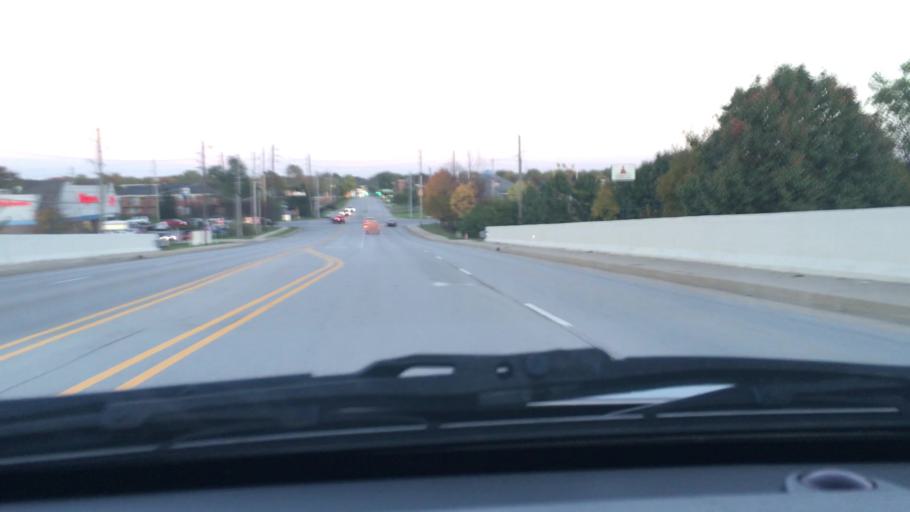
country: US
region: Indiana
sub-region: Marion County
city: Lawrence
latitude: 39.8907
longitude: -86.0484
